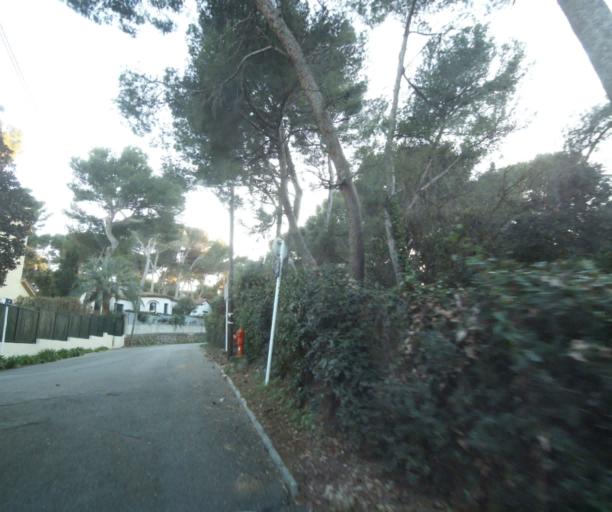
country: FR
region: Provence-Alpes-Cote d'Azur
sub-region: Departement des Alpes-Maritimes
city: Antibes
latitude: 43.5681
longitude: 7.1357
